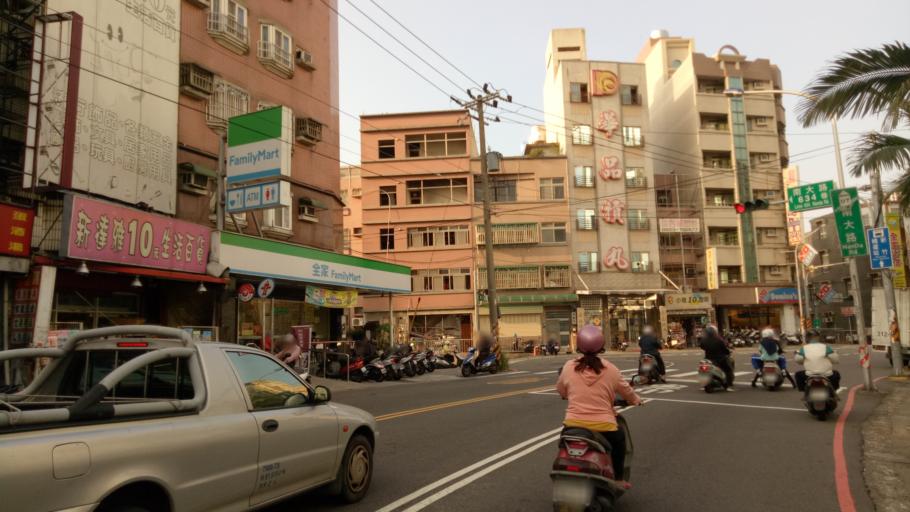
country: TW
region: Taiwan
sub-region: Hsinchu
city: Hsinchu
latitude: 24.7928
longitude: 120.9628
